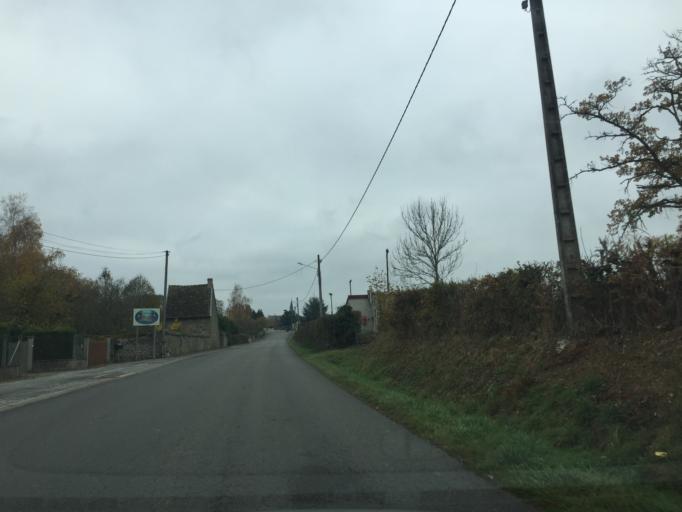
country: FR
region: Limousin
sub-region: Departement de la Creuse
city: Gouzon
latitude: 46.1184
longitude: 2.1805
